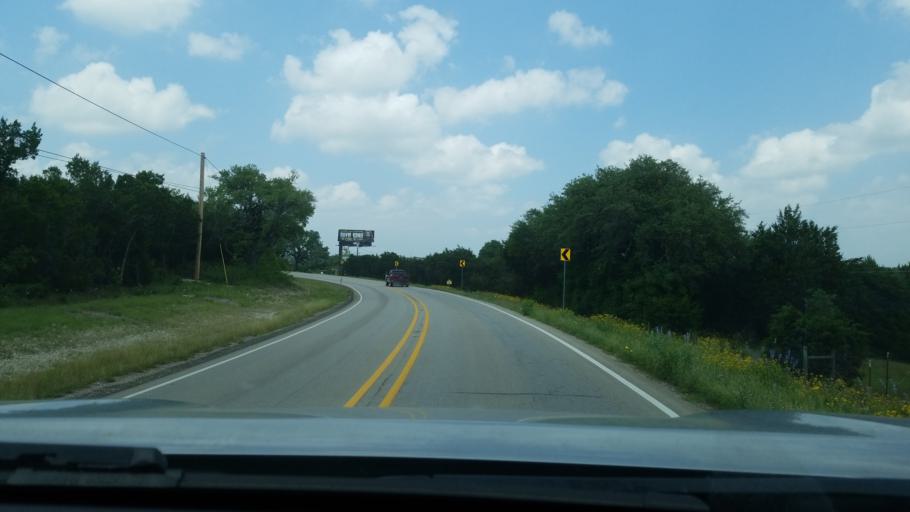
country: US
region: Texas
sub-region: Hays County
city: Dripping Springs
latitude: 30.1447
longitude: -98.0317
